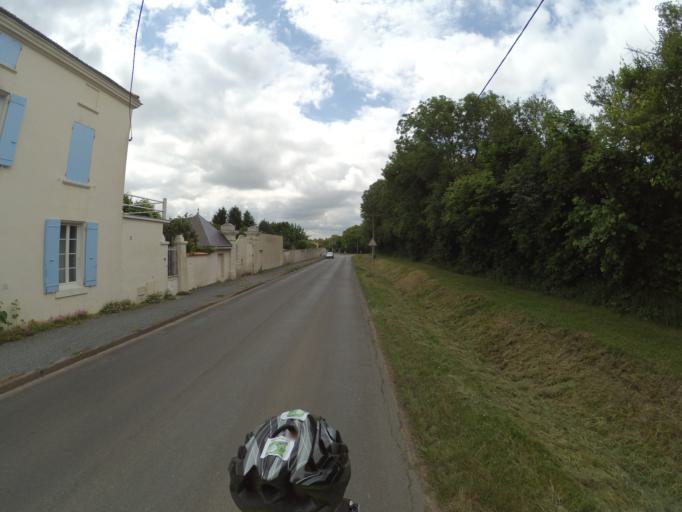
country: FR
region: Poitou-Charentes
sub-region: Departement de la Charente-Maritime
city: Breuil-Magne
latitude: 45.9593
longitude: -0.9695
